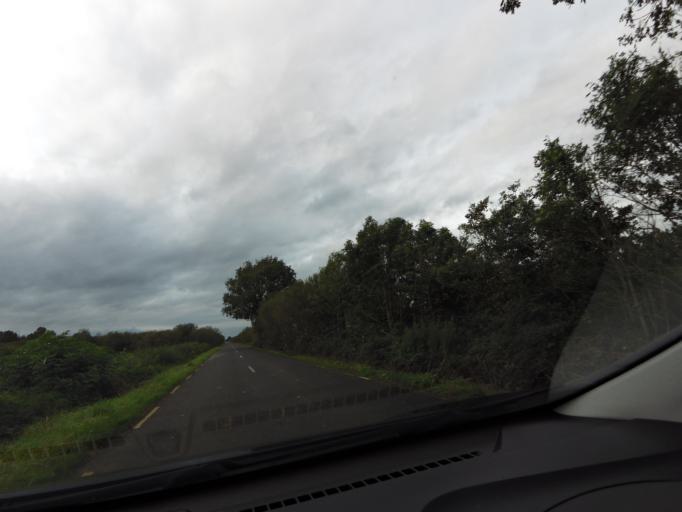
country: IE
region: Leinster
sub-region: Uibh Fhaili
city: Ferbane
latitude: 53.2040
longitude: -7.7840
